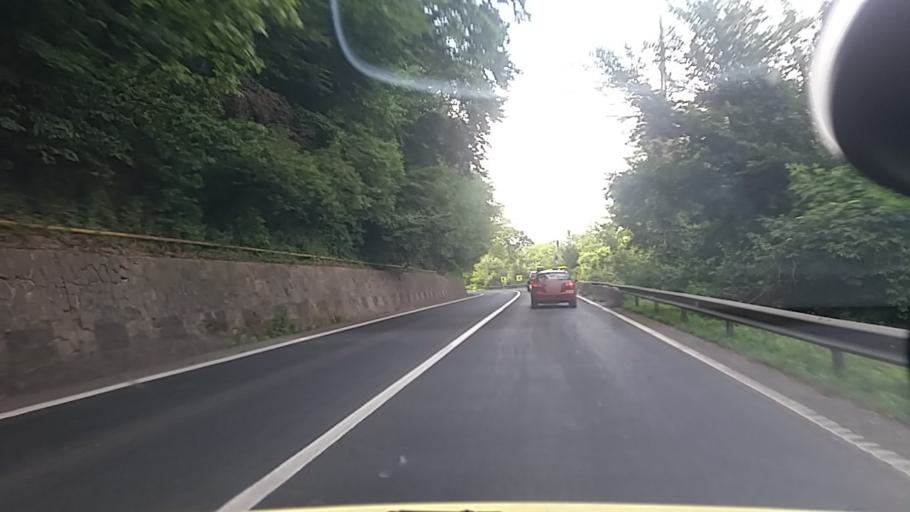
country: RO
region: Hunedoara
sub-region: Comuna Branisca
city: Branisca
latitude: 45.9068
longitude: 22.7757
